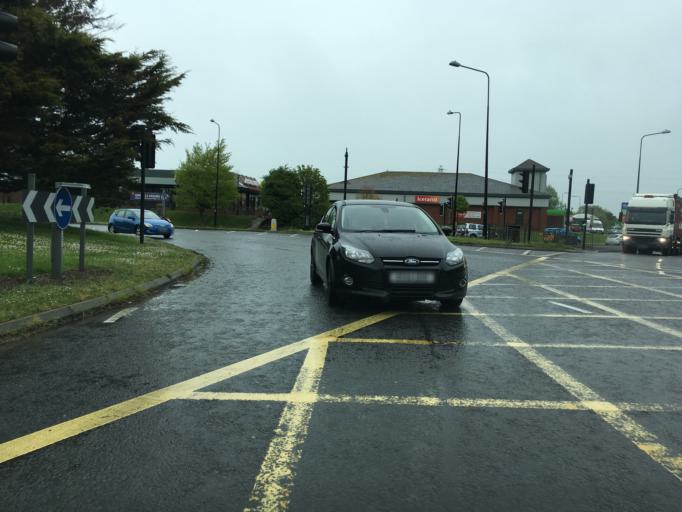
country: GB
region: England
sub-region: North Somerset
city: Weston-super-Mare
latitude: 51.3387
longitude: -2.9580
